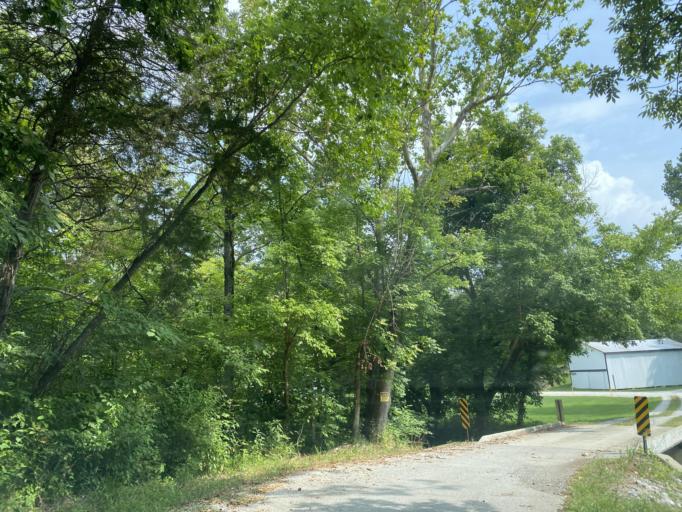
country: US
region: Kentucky
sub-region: Pendleton County
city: Falmouth
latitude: 38.8016
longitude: -84.2999
